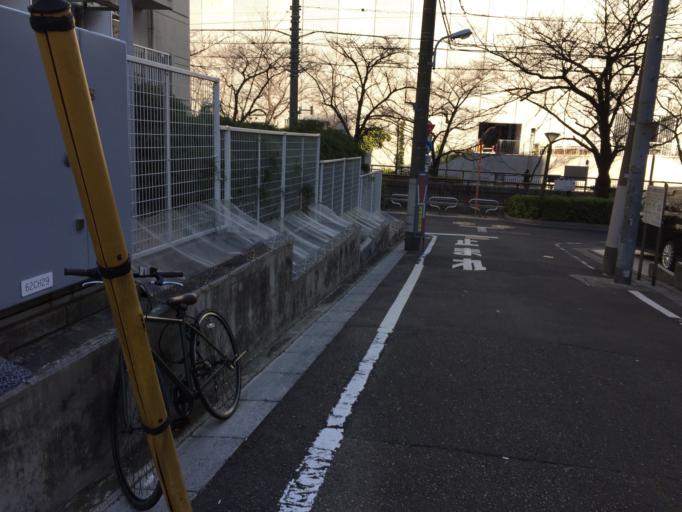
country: JP
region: Tokyo
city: Tokyo
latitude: 35.6498
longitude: 139.6874
